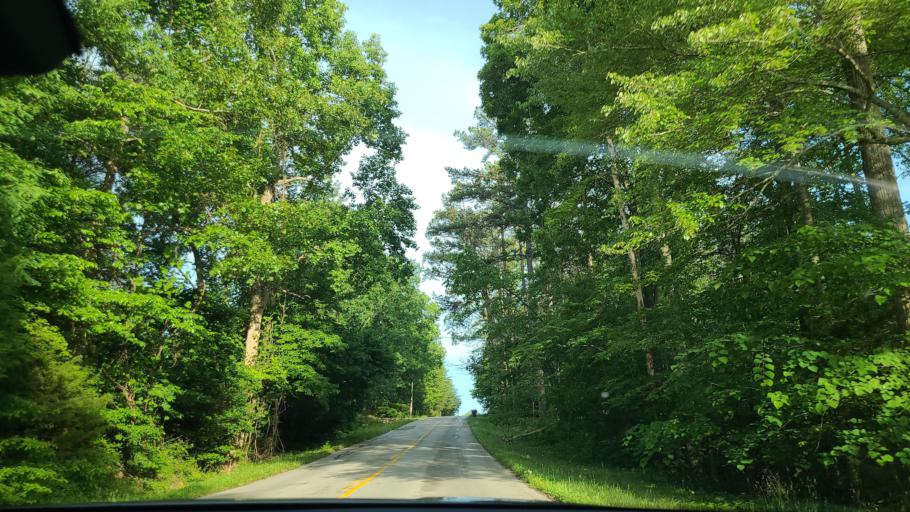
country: US
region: Kentucky
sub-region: Whitley County
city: Corbin
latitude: 36.8870
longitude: -84.2154
